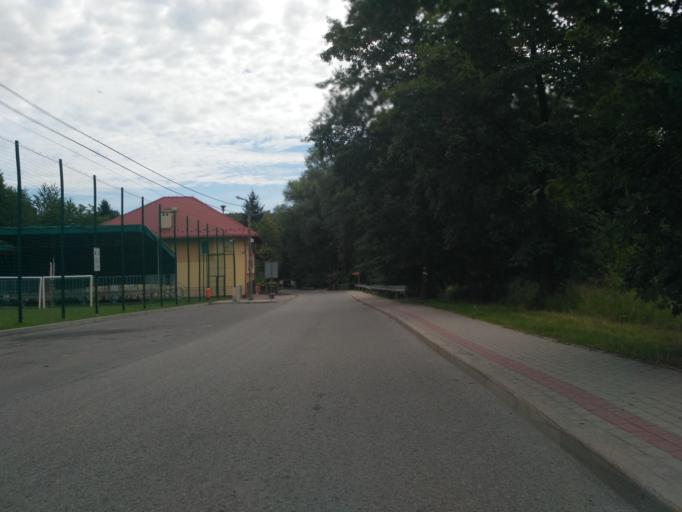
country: PL
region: Subcarpathian Voivodeship
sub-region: Powiat rzeszowski
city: Straszydle
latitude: 49.8991
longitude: 21.9506
